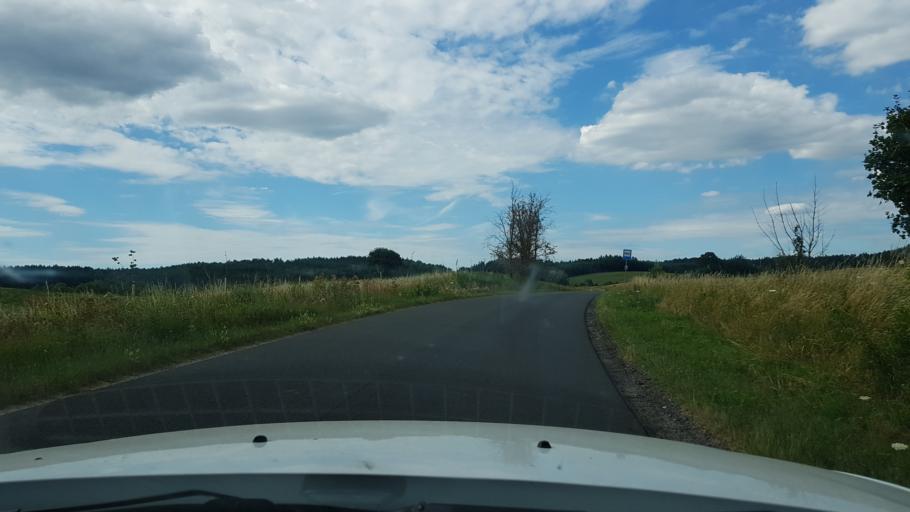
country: PL
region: West Pomeranian Voivodeship
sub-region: Powiat drawski
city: Wierzchowo
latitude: 53.4827
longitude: 16.0452
